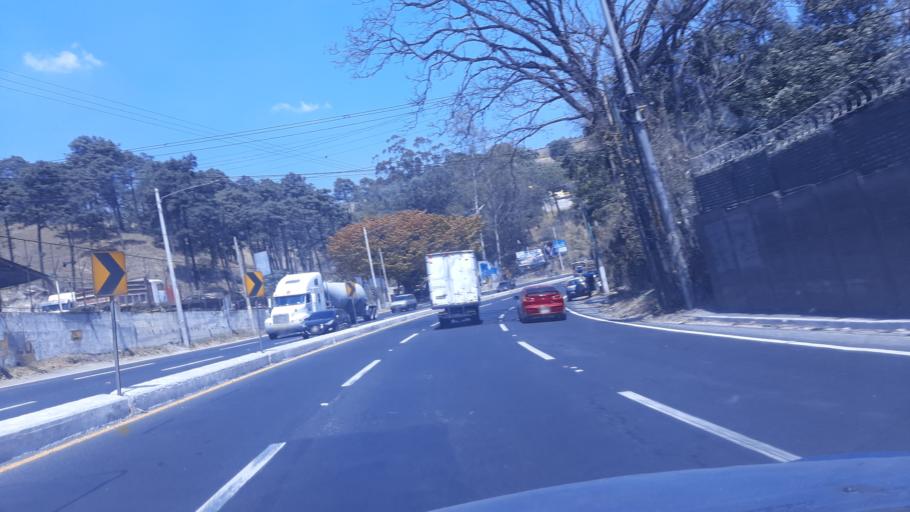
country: GT
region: Guatemala
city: Amatitlan
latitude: 14.4941
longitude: -90.6284
